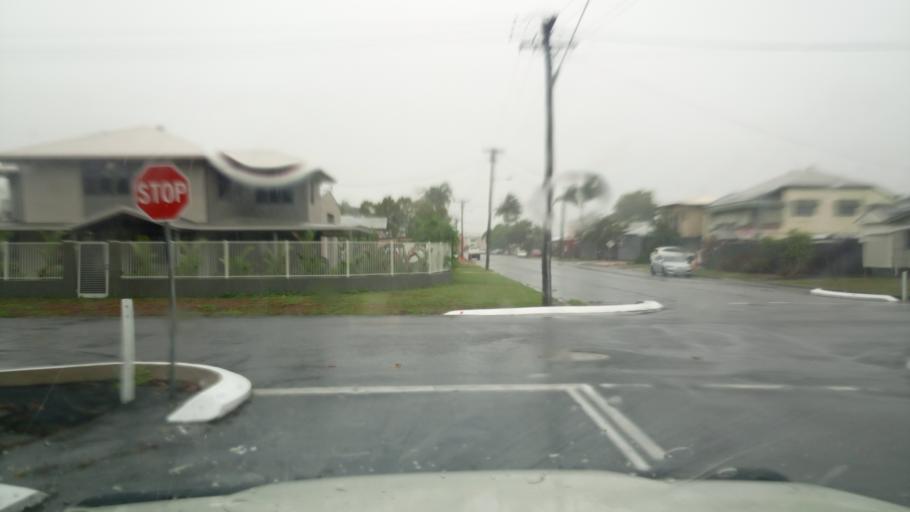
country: AU
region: Queensland
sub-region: Cairns
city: Cairns
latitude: -16.9376
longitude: 145.7614
